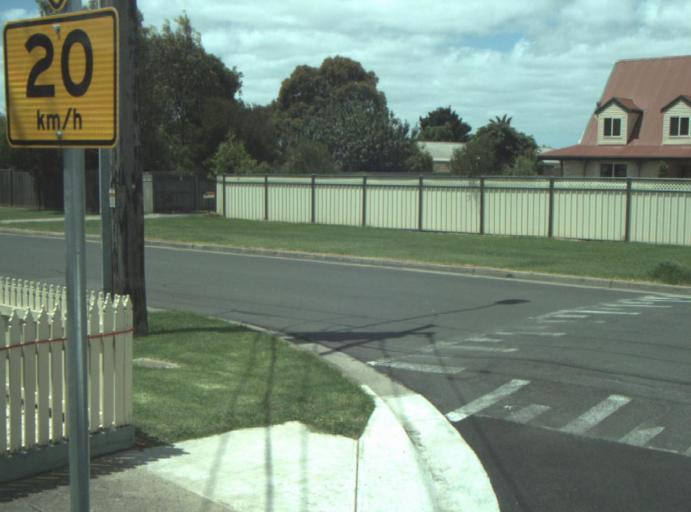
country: AU
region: Victoria
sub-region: Greater Geelong
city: Breakwater
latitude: -38.1889
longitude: 144.3490
